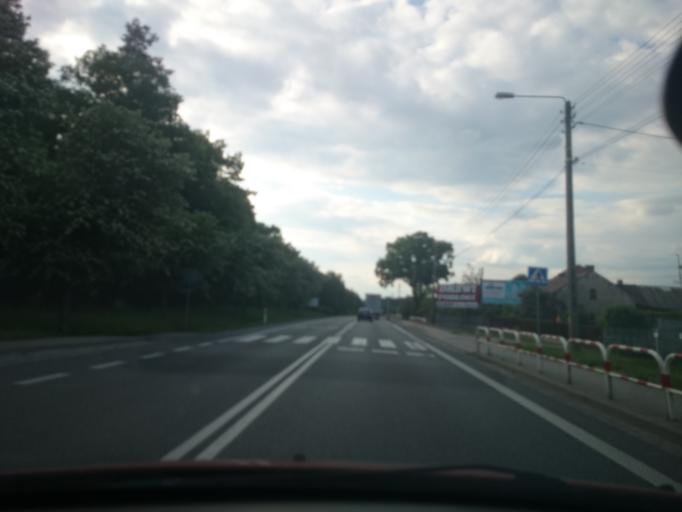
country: PL
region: Opole Voivodeship
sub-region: Powiat opolski
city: Tarnow Opolski
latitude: 50.6068
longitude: 18.0734
